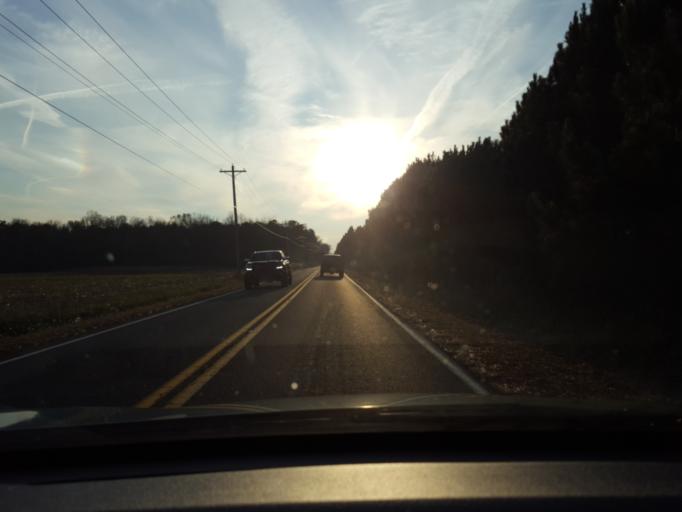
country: US
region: Maryland
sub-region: Charles County
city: Hughesville
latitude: 38.5197
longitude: -76.8437
